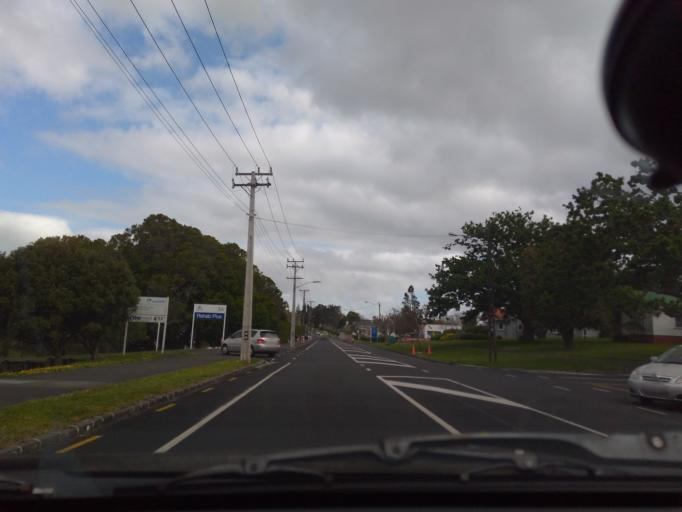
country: NZ
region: Auckland
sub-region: Auckland
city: Rosebank
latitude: -36.8737
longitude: 174.7101
